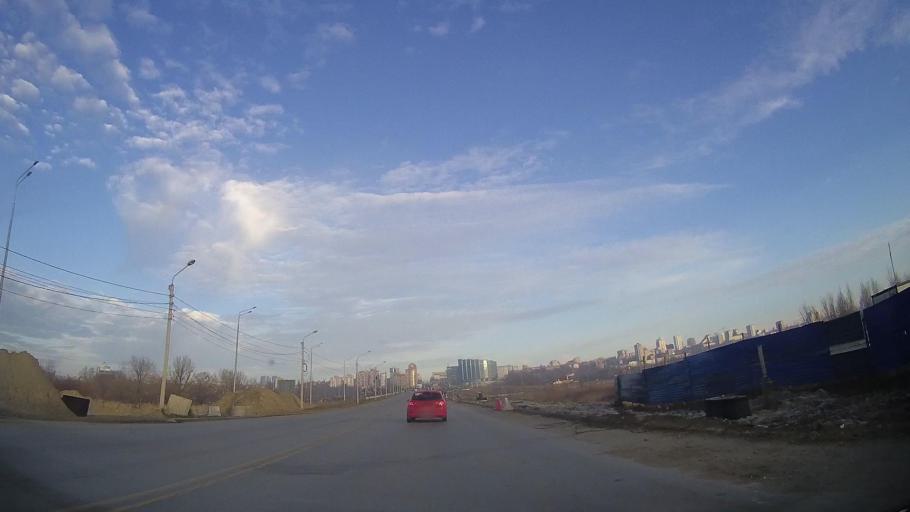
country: RU
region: Rostov
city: Rostov-na-Donu
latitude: 47.2072
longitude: 39.7258
